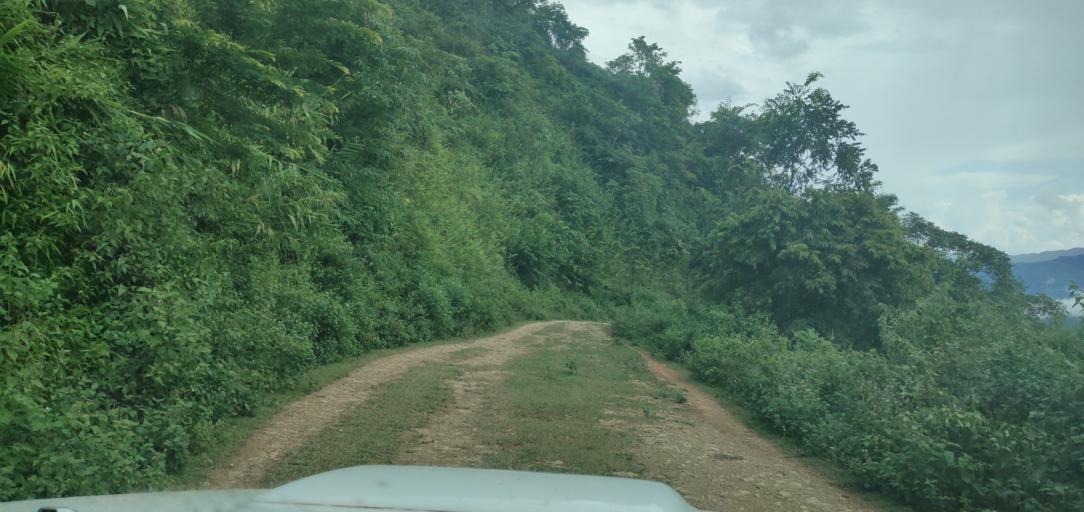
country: LA
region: Phongsali
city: Phongsali
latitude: 21.4432
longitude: 102.3163
